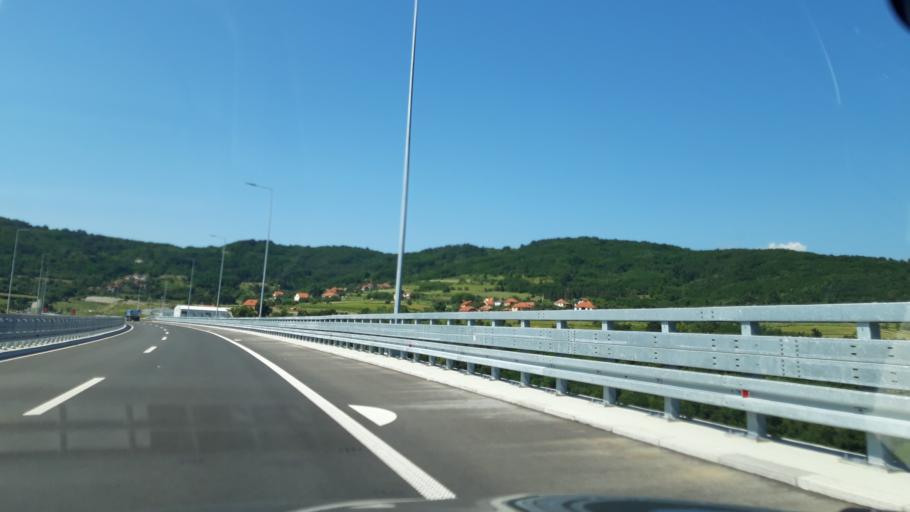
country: RS
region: Central Serbia
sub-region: Pcinjski Okrug
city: Vladicin Han
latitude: 42.7223
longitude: 22.0765
